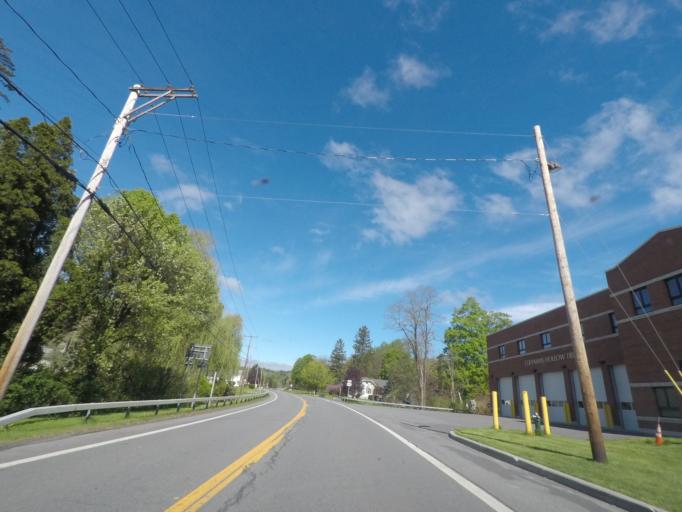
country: US
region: New York
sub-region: Albany County
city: Ravena
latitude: 42.4716
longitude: -73.8950
